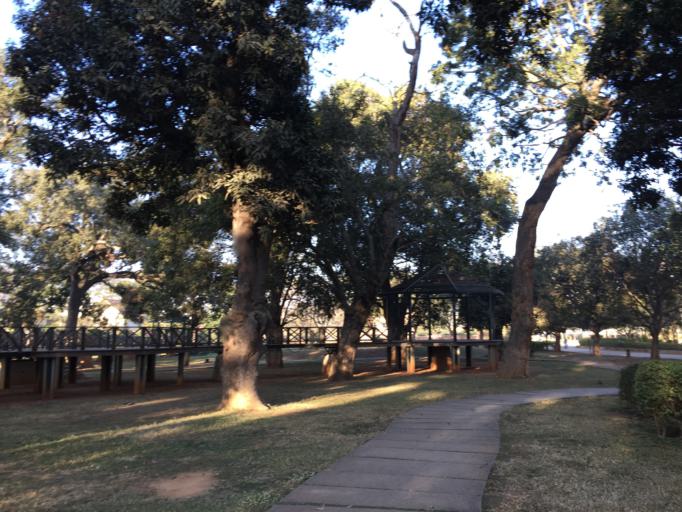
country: IN
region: Karnataka
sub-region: Bangalore Urban
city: Yelahanka
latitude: 13.0554
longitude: 77.6214
